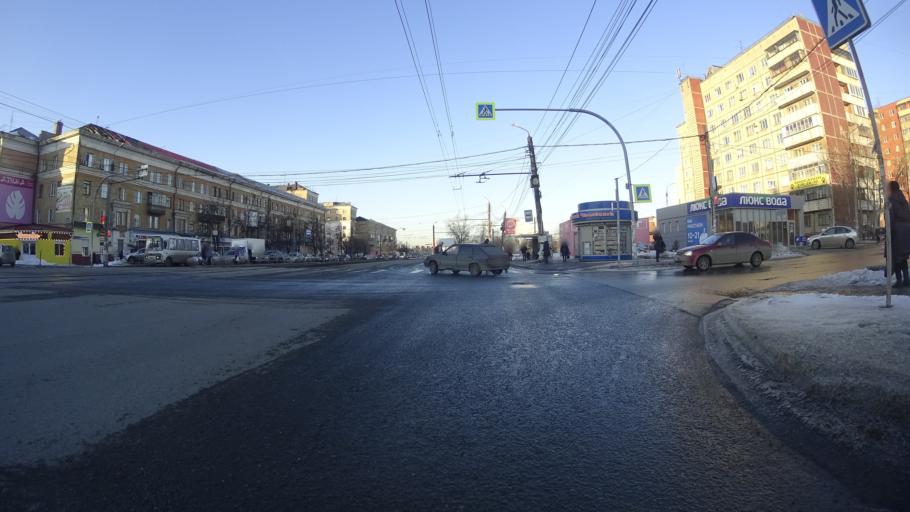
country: RU
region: Chelyabinsk
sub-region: Gorod Chelyabinsk
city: Chelyabinsk
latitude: 55.1439
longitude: 61.4441
